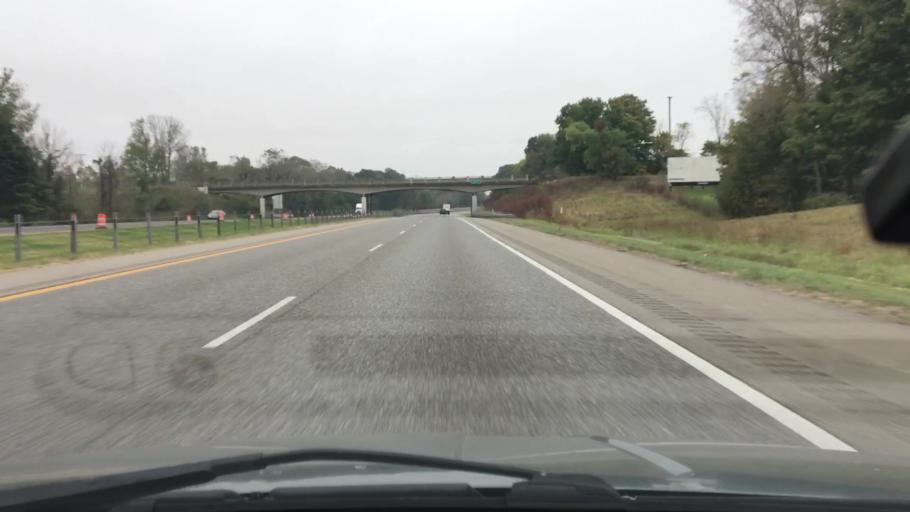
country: US
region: Michigan
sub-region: Van Buren County
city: Decatur
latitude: 42.1921
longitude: -85.9913
